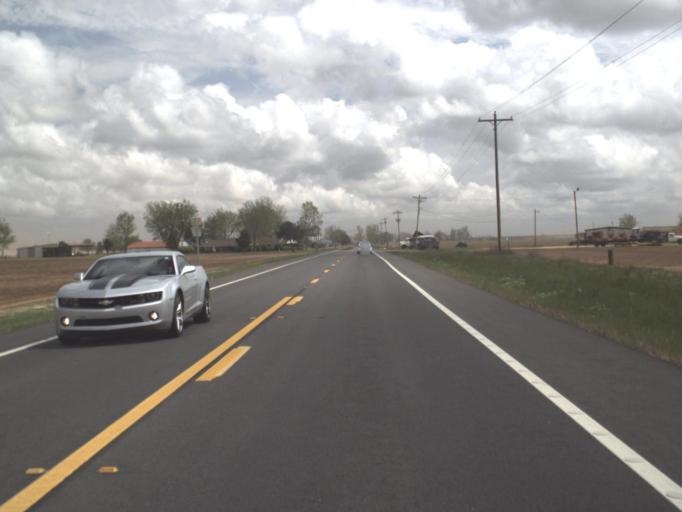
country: US
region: Florida
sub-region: Escambia County
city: Century
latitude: 30.8946
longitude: -87.1665
